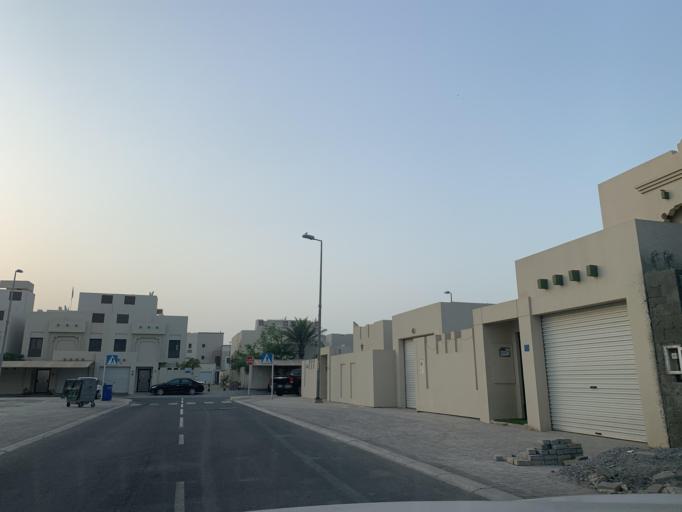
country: BH
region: Manama
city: Jidd Hafs
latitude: 26.2235
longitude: 50.4481
